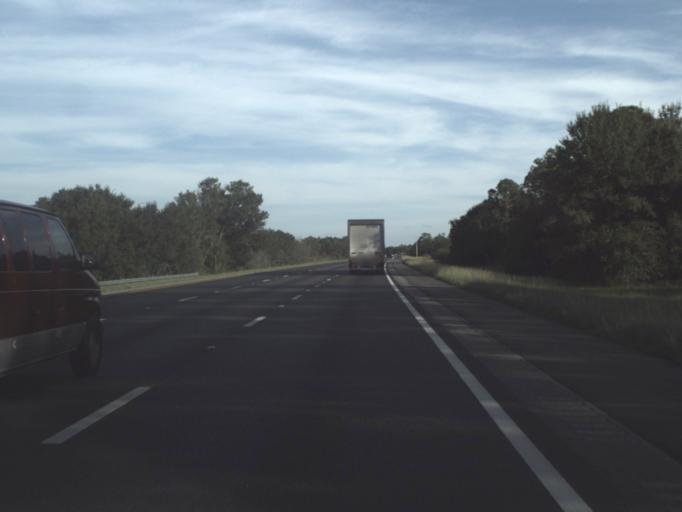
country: US
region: Florida
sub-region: Lee County
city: Suncoast Estates
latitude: 26.7911
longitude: -81.9066
